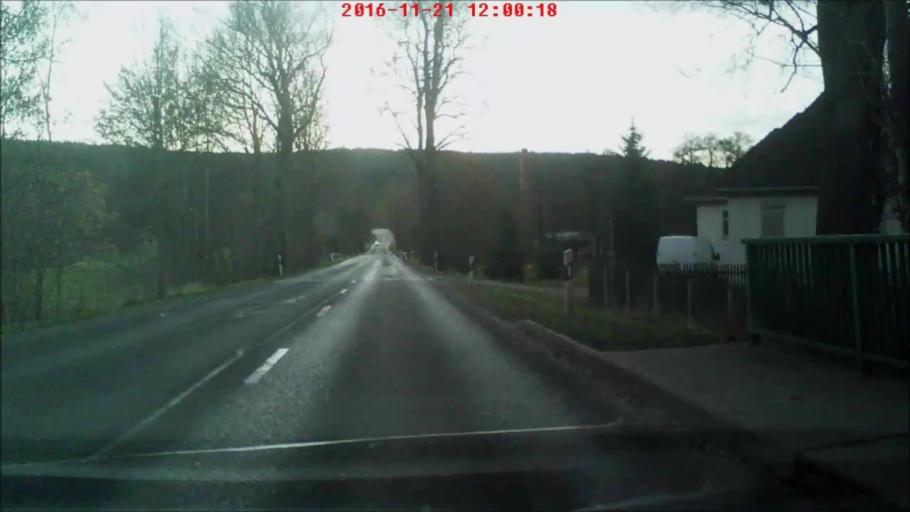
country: DE
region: Thuringia
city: Schleusingen
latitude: 50.5023
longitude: 10.7417
